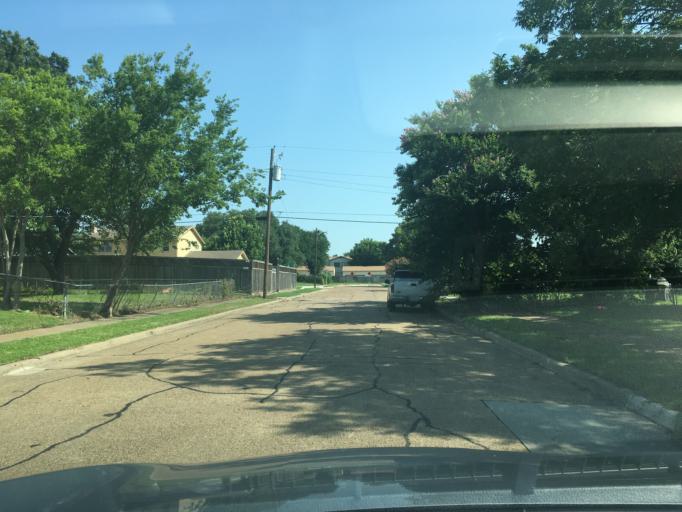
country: US
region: Texas
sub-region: Dallas County
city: Richardson
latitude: 32.9280
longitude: -96.6973
